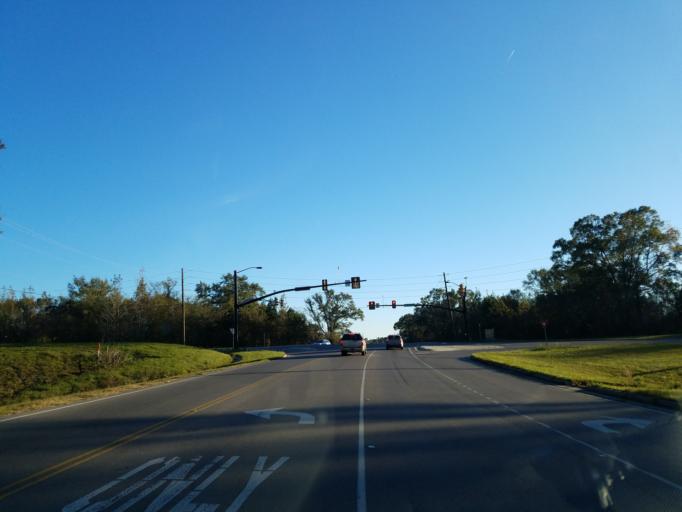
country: US
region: Mississippi
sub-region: Lamar County
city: Arnold Line
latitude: 31.3392
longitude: -89.3986
